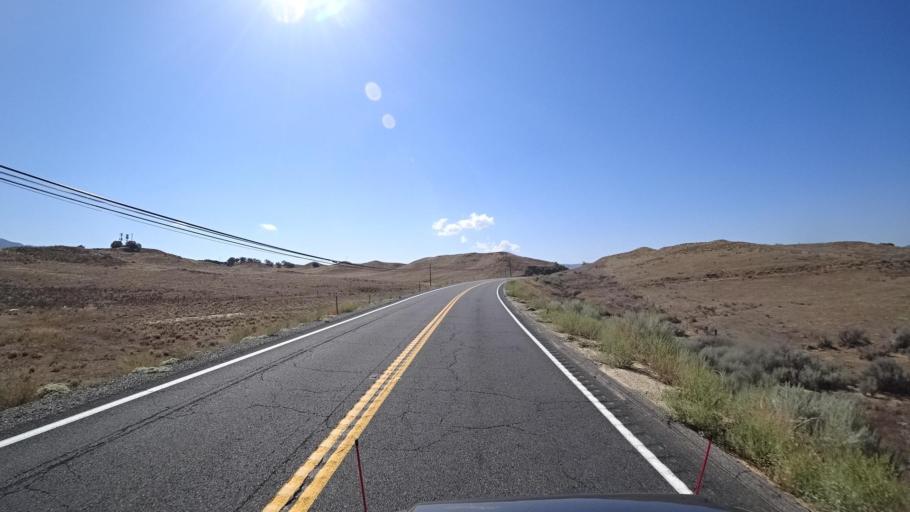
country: US
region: California
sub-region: Riverside County
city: Aguanga
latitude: 33.3060
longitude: -116.6917
